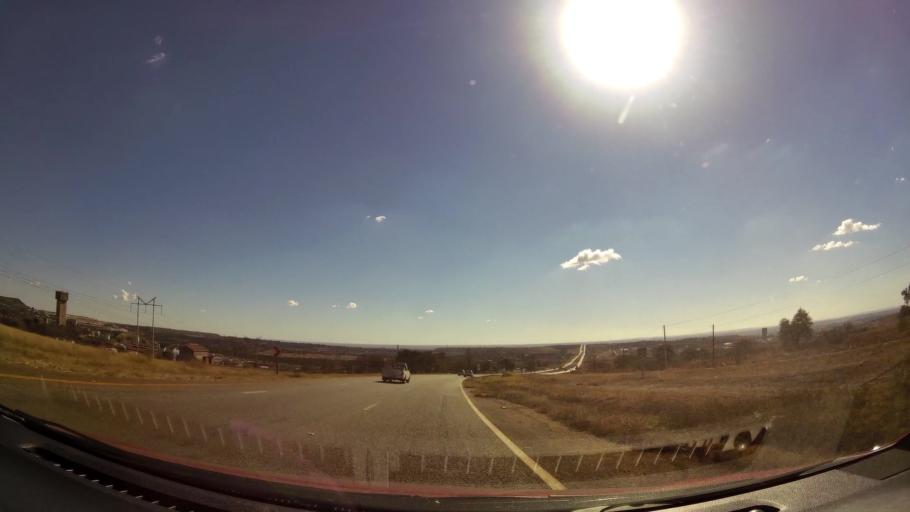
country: ZA
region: Gauteng
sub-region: West Rand District Municipality
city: Carletonville
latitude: -26.4148
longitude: 27.4343
